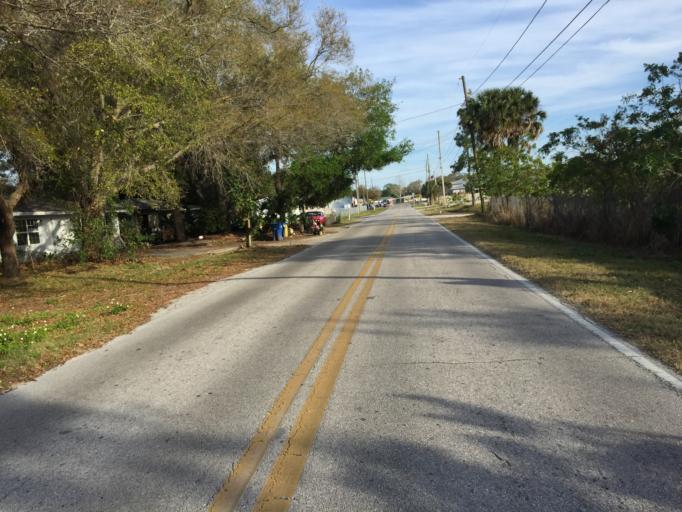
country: US
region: Florida
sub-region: Pinellas County
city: Clearwater
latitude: 27.9845
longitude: -82.7864
